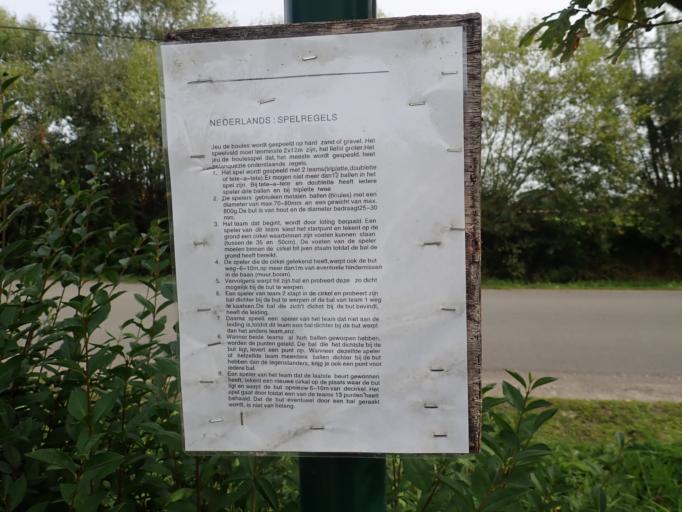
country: BE
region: Flanders
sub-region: Provincie Antwerpen
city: Bornem
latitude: 51.0829
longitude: 4.2358
